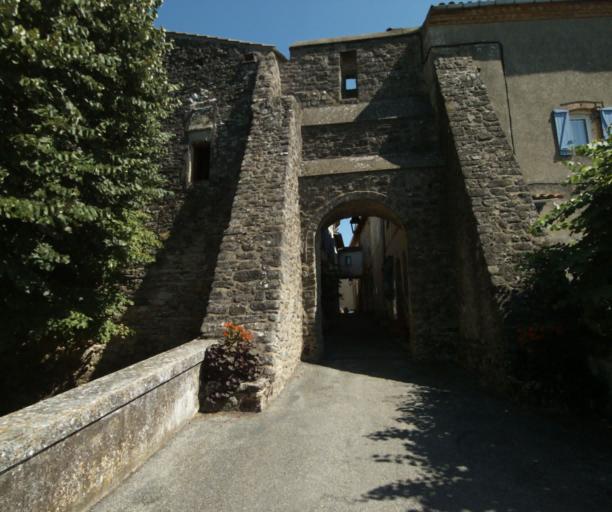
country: FR
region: Midi-Pyrenees
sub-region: Departement de la Haute-Garonne
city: Saint-Felix-Lauragais
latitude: 43.4902
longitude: 1.8971
